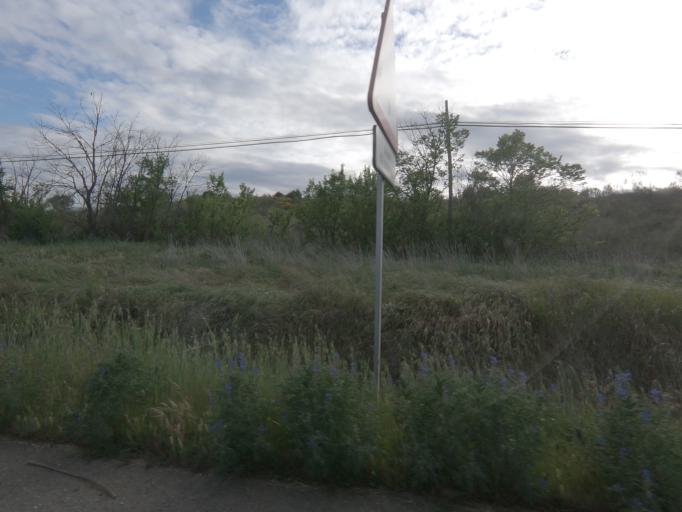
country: ES
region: Extremadura
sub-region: Provincia de Caceres
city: Coria
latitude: 40.0040
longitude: -6.5529
